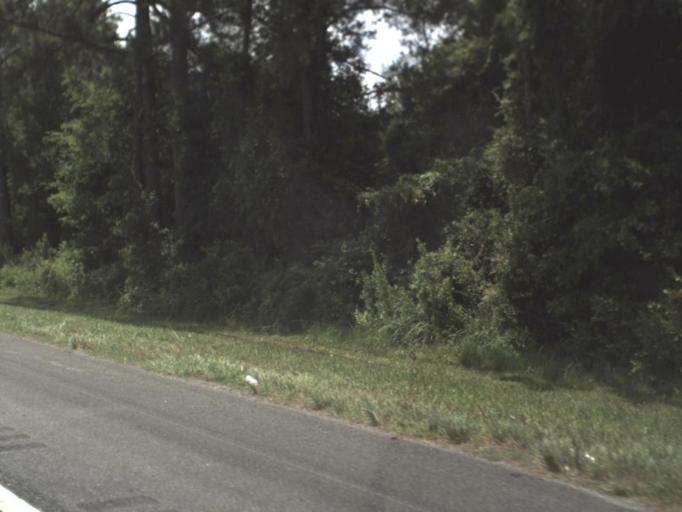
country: US
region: Florida
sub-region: Columbia County
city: Lake City
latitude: 30.1538
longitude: -82.6755
